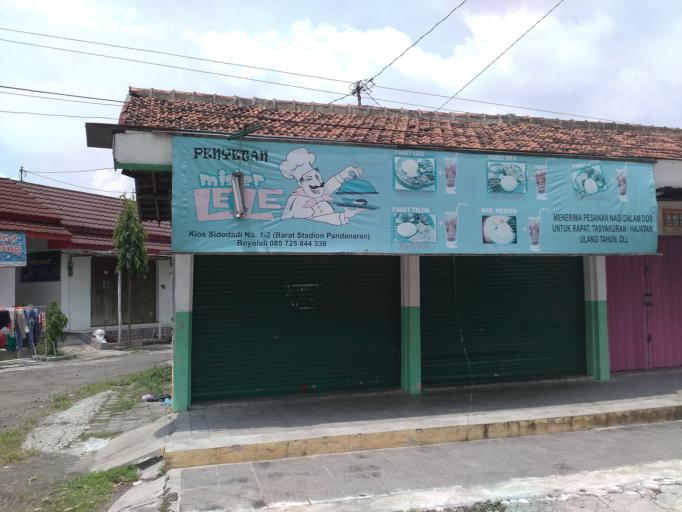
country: ID
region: Central Java
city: Boyolali
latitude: -7.5443
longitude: 110.6015
